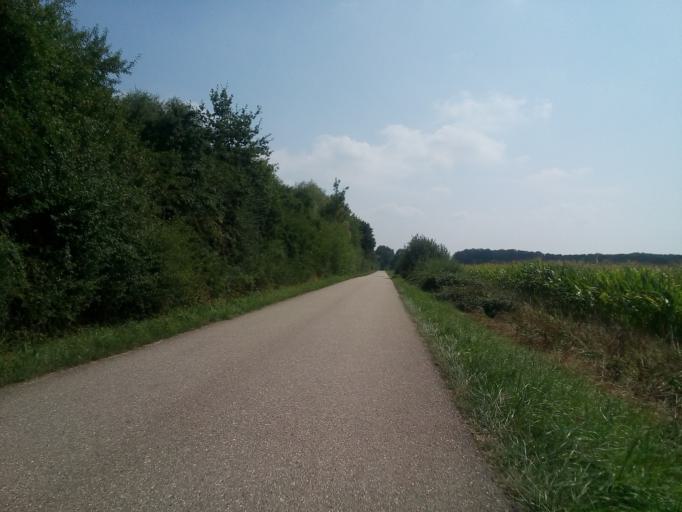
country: DE
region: Baden-Wuerttemberg
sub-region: Freiburg Region
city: Willstatt
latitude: 48.5947
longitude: 7.8879
